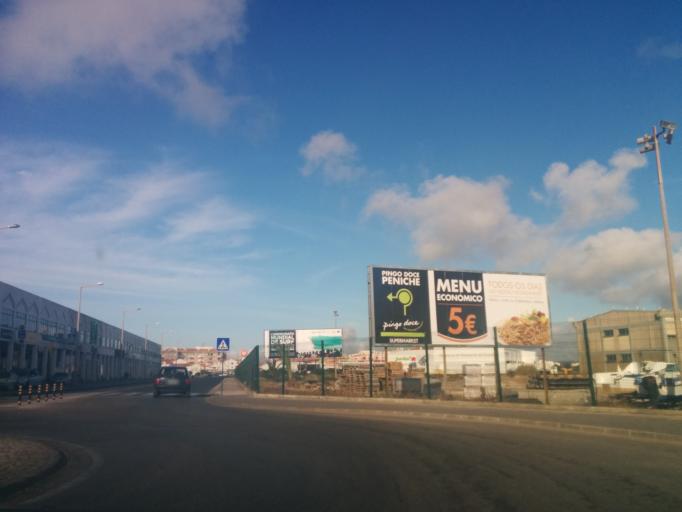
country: PT
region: Leiria
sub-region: Peniche
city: Peniche
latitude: 39.3580
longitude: -9.3735
